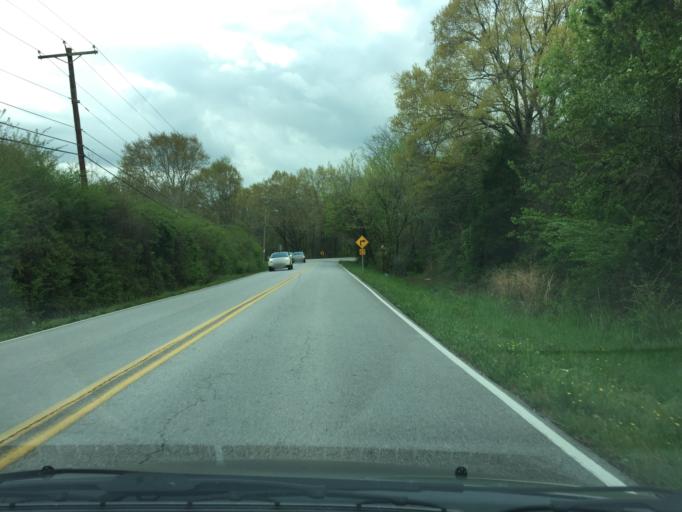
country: US
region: Tennessee
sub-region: Hamilton County
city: Falling Water
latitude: 35.1487
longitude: -85.2392
